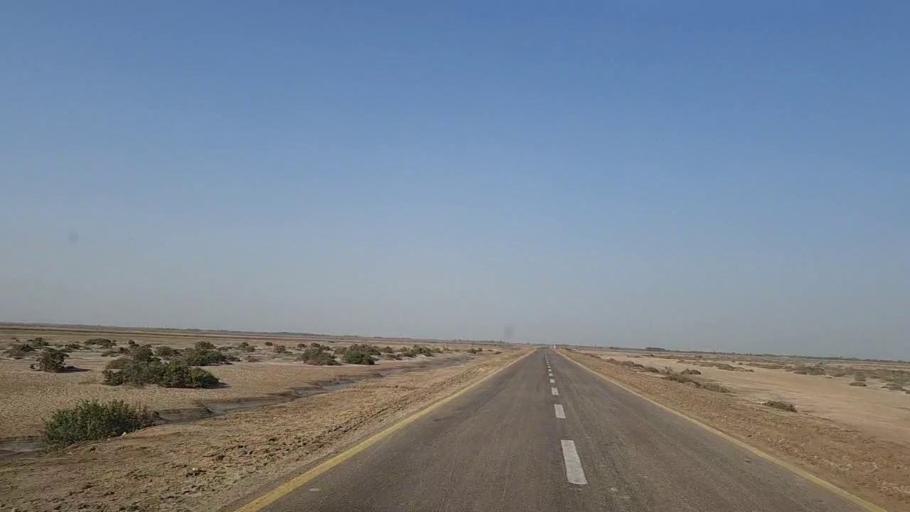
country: PK
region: Sindh
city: Jati
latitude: 24.4919
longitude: 68.3755
